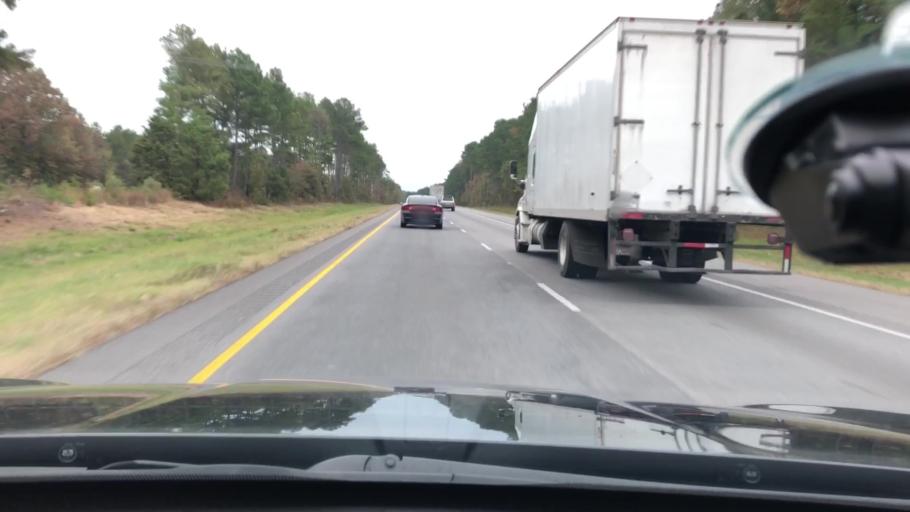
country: US
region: Arkansas
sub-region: Hempstead County
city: Hope
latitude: 33.6272
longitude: -93.7432
